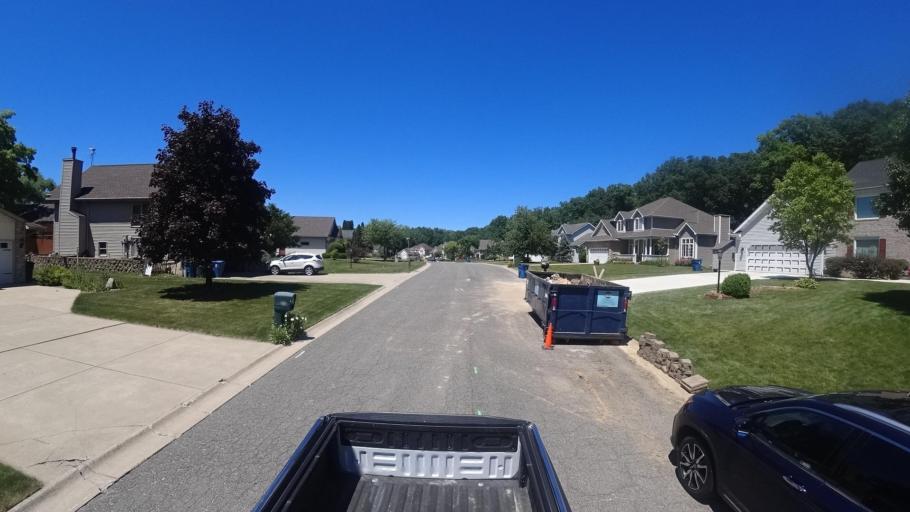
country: US
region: Indiana
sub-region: Porter County
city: Porter
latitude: 41.6321
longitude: -87.0729
